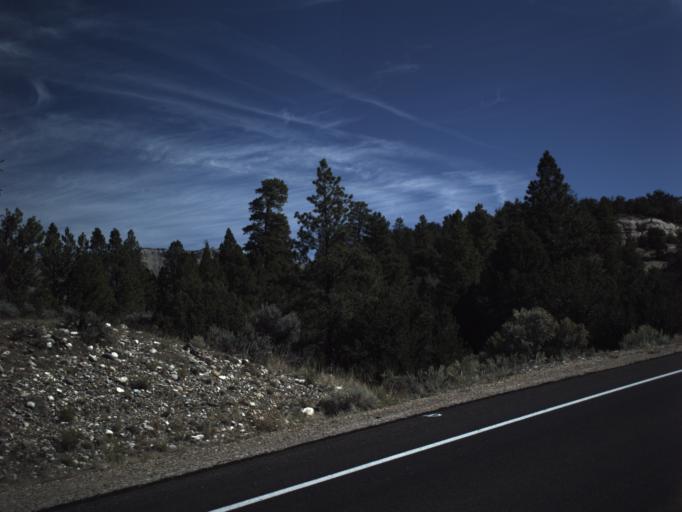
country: US
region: Utah
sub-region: Garfield County
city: Panguitch
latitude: 37.6166
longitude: -111.8927
